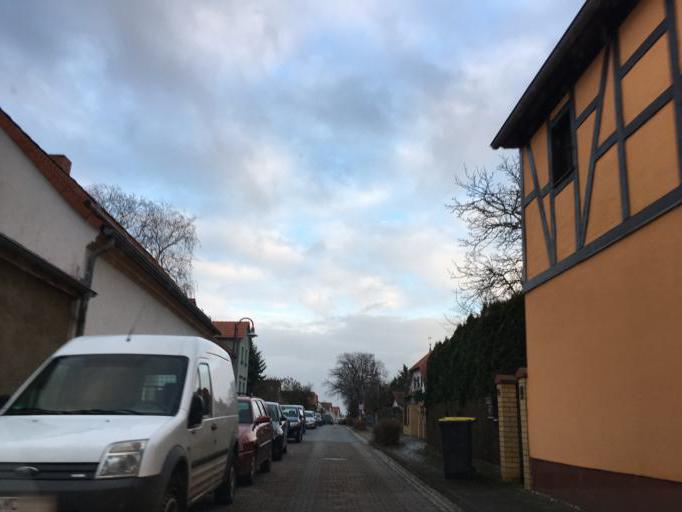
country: DE
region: Saxony
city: Espenhain
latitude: 51.2204
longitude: 12.4655
